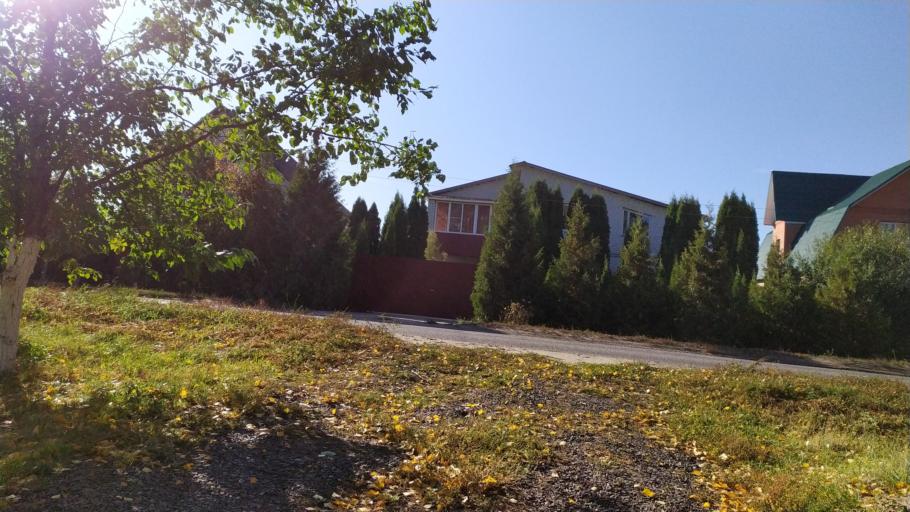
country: RU
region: Kursk
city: Kursk
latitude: 51.6429
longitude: 36.1394
